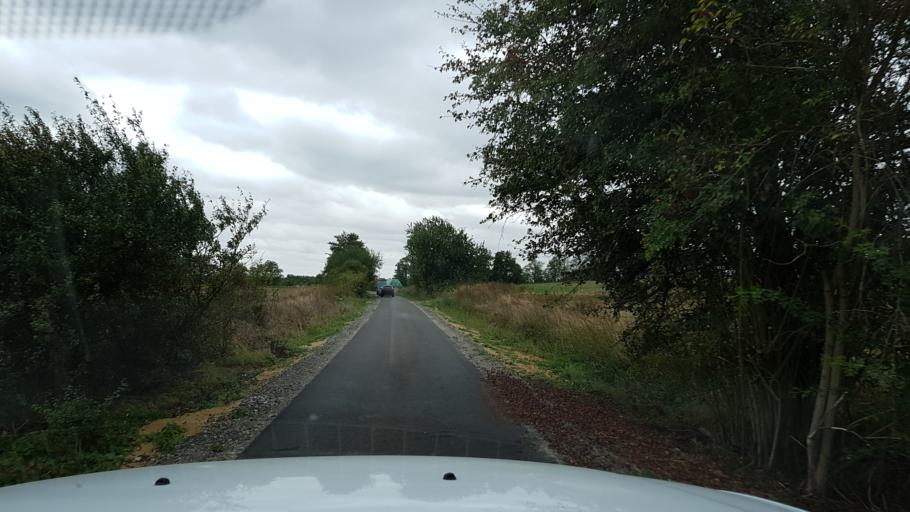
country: PL
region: West Pomeranian Voivodeship
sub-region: Powiat gryfinski
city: Cedynia
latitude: 52.8595
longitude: 14.2839
